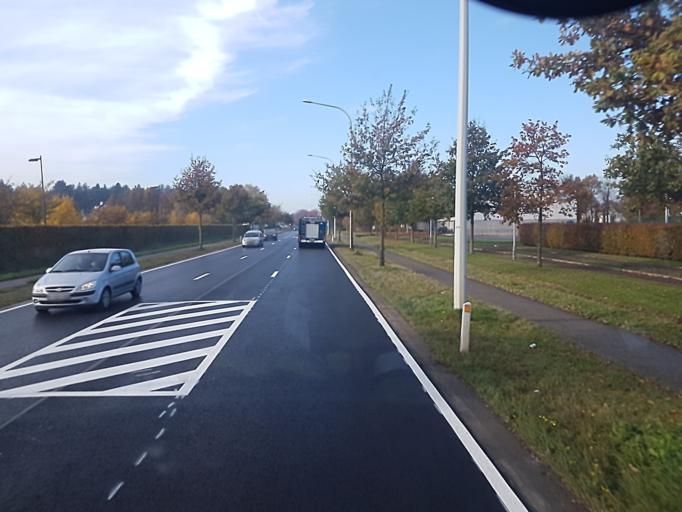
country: BE
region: Flanders
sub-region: Provincie Antwerpen
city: Beerse
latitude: 51.3090
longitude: 4.8461
